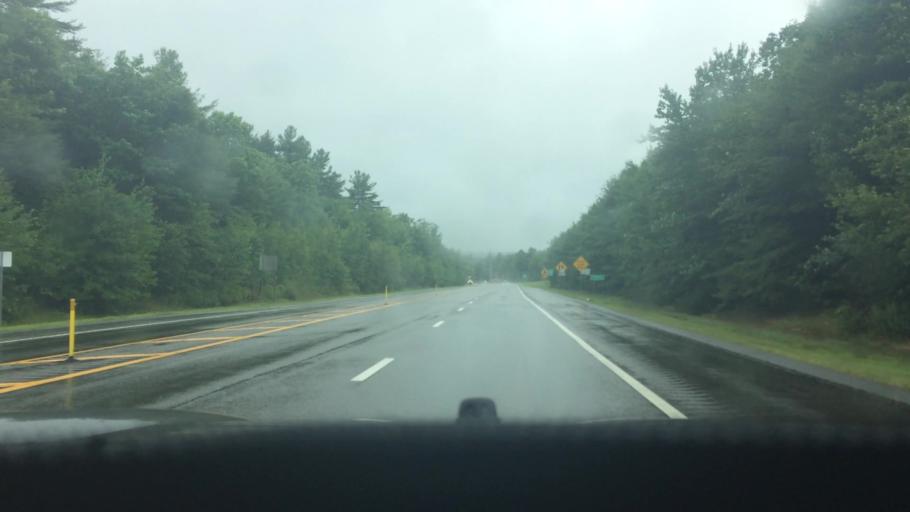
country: US
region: Massachusetts
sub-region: Worcester County
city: Westminster
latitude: 42.5678
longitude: -71.9452
